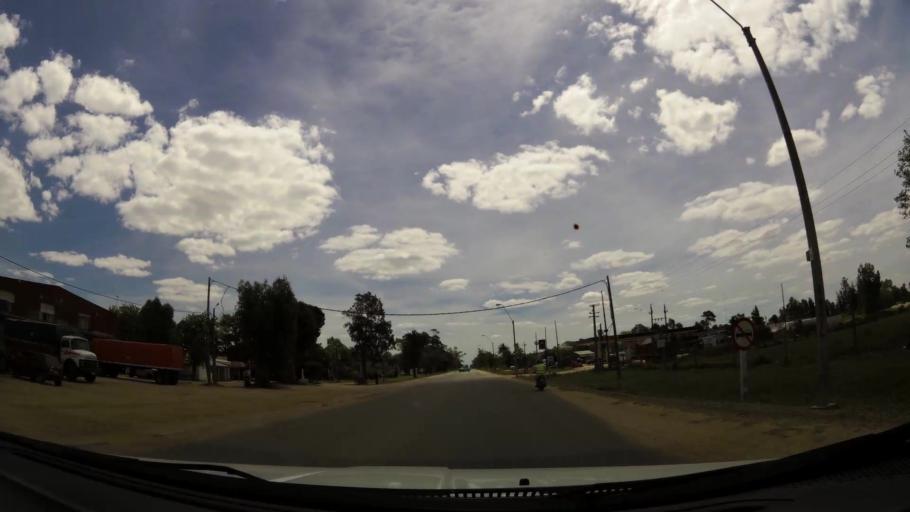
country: UY
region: San Jose
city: Delta del Tigre
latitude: -34.7382
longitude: -56.4412
